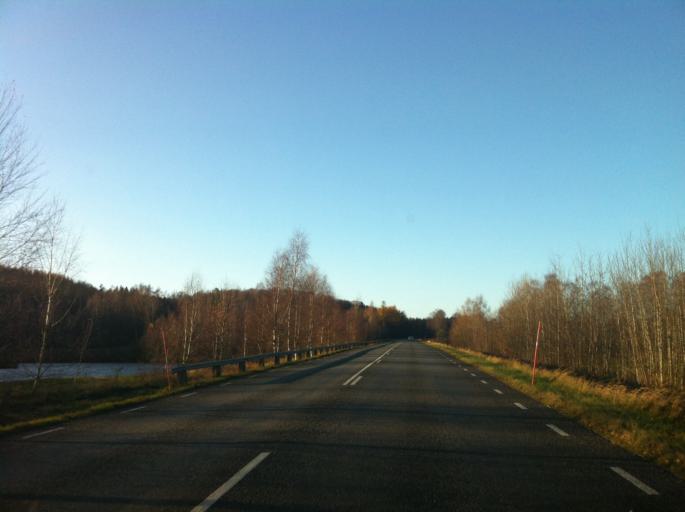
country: SE
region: Skane
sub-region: Kristianstads Kommun
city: Tollarp
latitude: 56.1868
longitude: 14.3465
